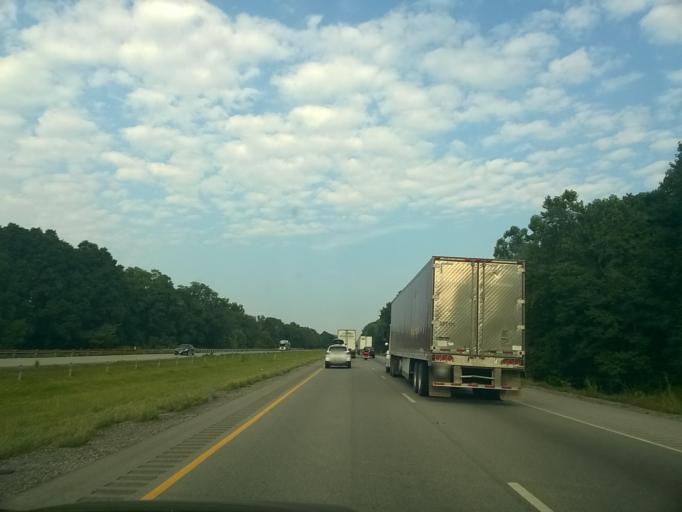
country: US
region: Indiana
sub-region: Putnam County
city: Cloverdale
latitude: 39.5312
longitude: -86.8593
